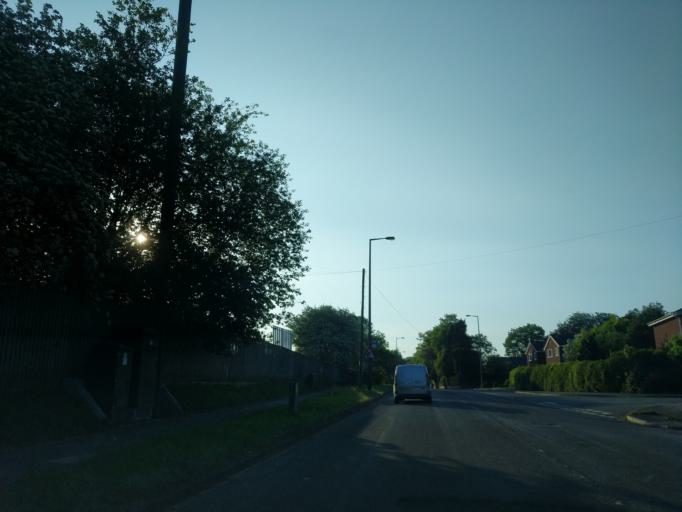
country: GB
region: England
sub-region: Staffordshire
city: Stone
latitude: 52.8977
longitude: -2.1366
